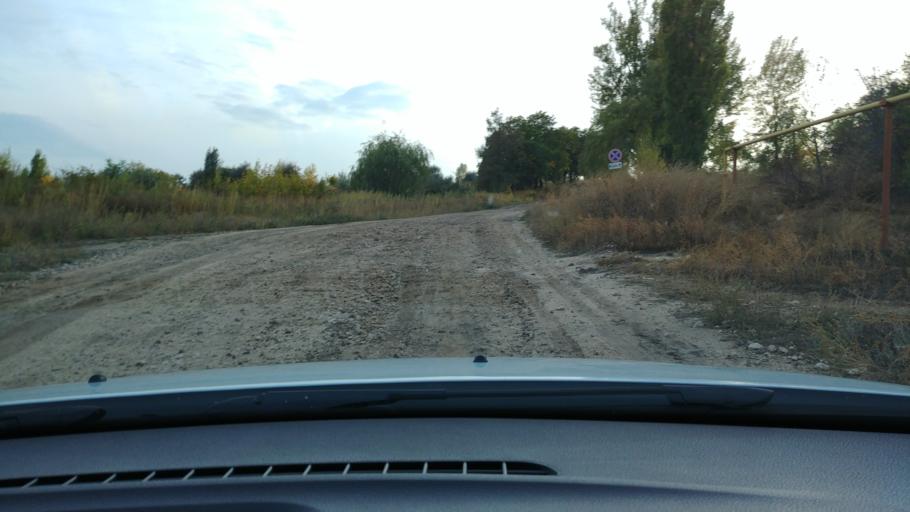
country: MD
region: Rezina
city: Saharna
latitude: 47.6817
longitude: 28.9735
